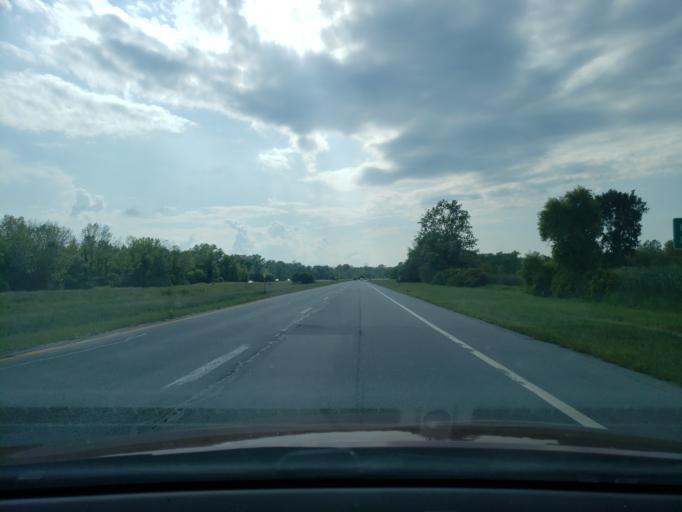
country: US
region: New York
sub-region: Monroe County
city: Greece
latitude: 43.2726
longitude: -77.6779
